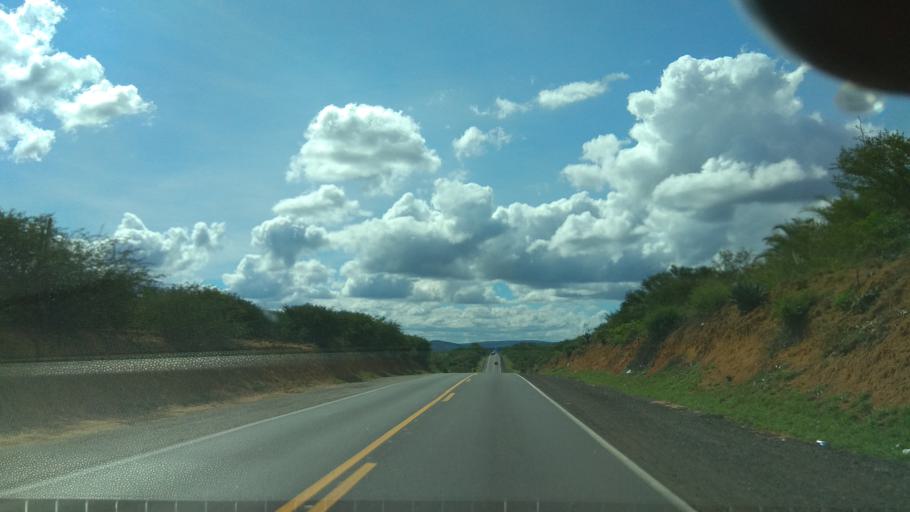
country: BR
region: Bahia
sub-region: Jaguaquara
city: Jaguaquara
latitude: -13.4318
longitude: -40.0287
